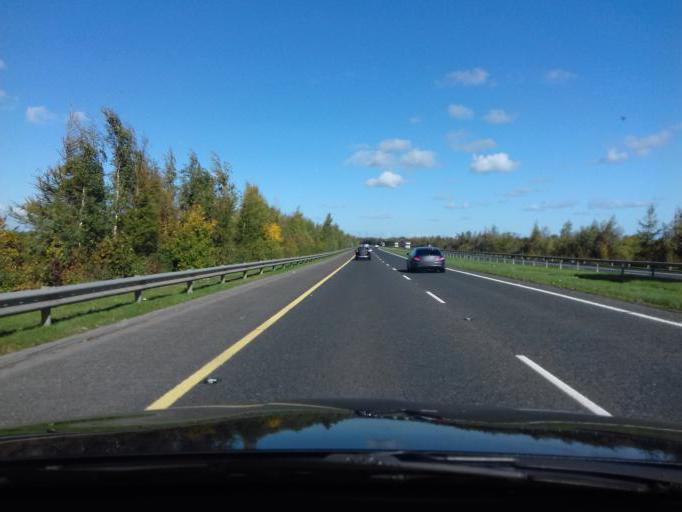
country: IE
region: Leinster
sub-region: Fingal County
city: Blanchardstown
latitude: 53.4480
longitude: -6.3558
